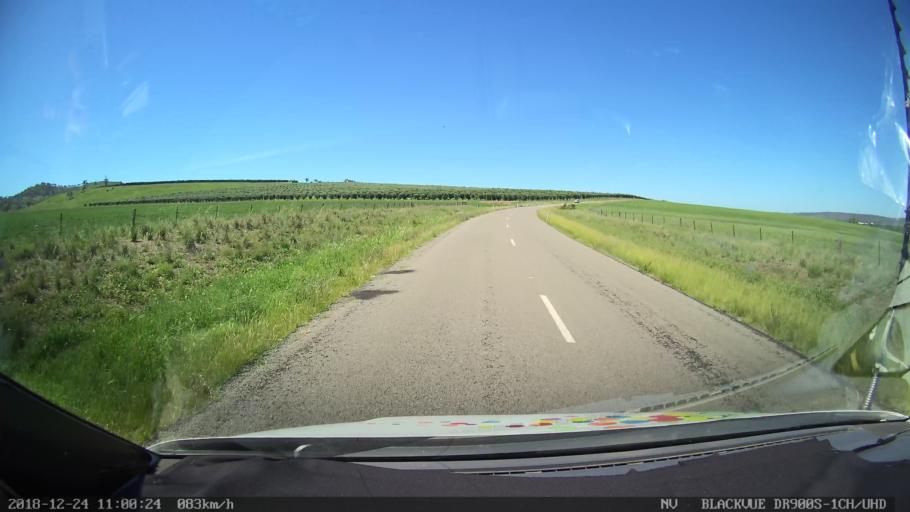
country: AU
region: New South Wales
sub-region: Upper Hunter Shire
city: Merriwa
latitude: -32.0672
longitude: 150.3941
